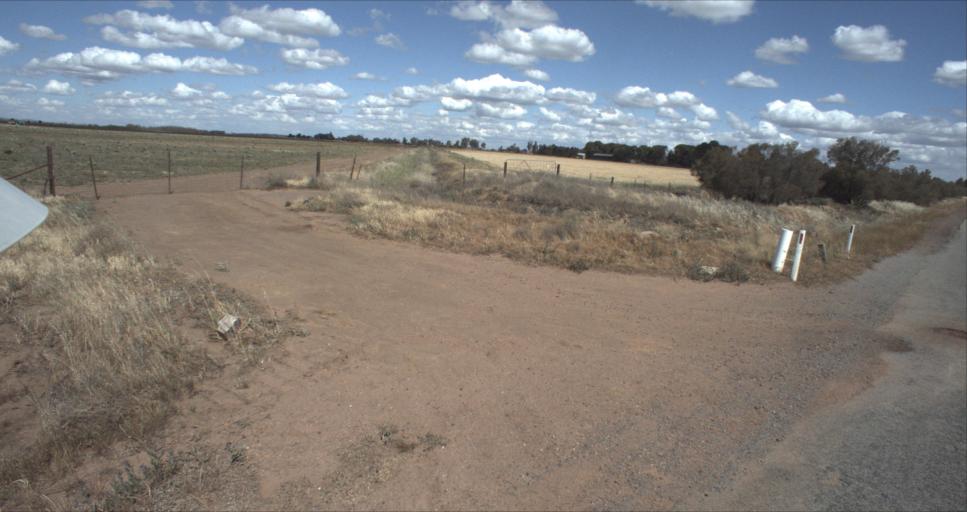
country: AU
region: New South Wales
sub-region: Leeton
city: Leeton
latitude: -34.4774
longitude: 146.2497
